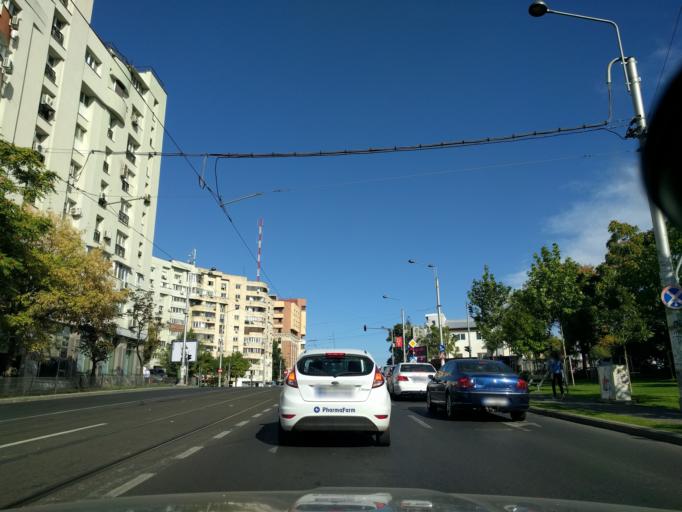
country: RO
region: Bucuresti
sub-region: Municipiul Bucuresti
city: Bucuresti
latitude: 44.4396
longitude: 26.0819
